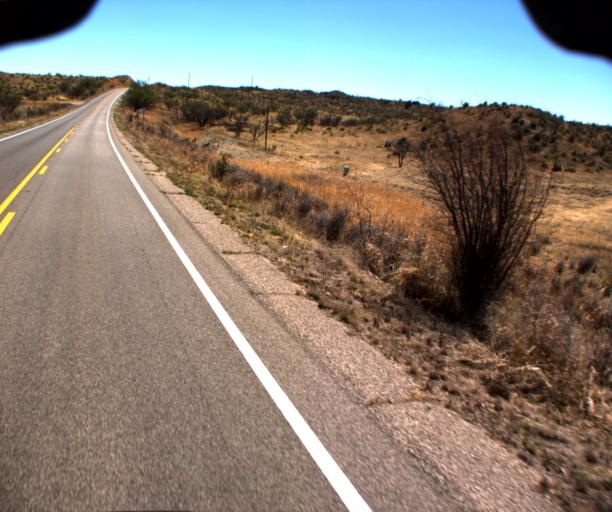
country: US
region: Arizona
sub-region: Pima County
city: Corona de Tucson
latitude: 31.7303
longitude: -110.6590
